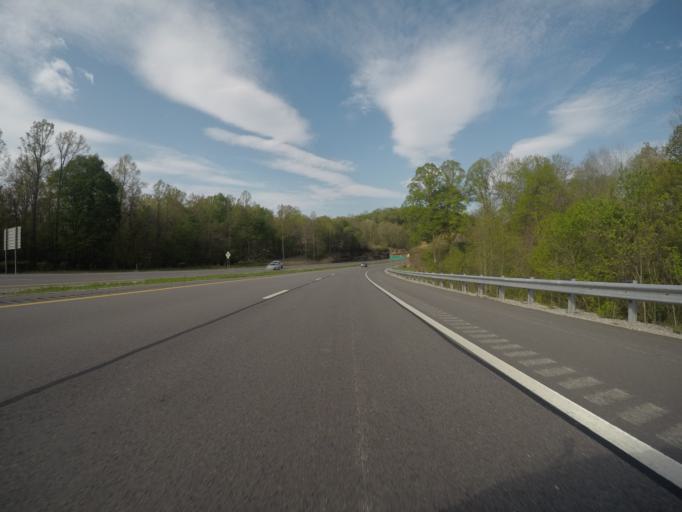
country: US
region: West Virginia
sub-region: Kanawha County
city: Alum Creek
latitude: 38.2672
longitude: -81.7903
